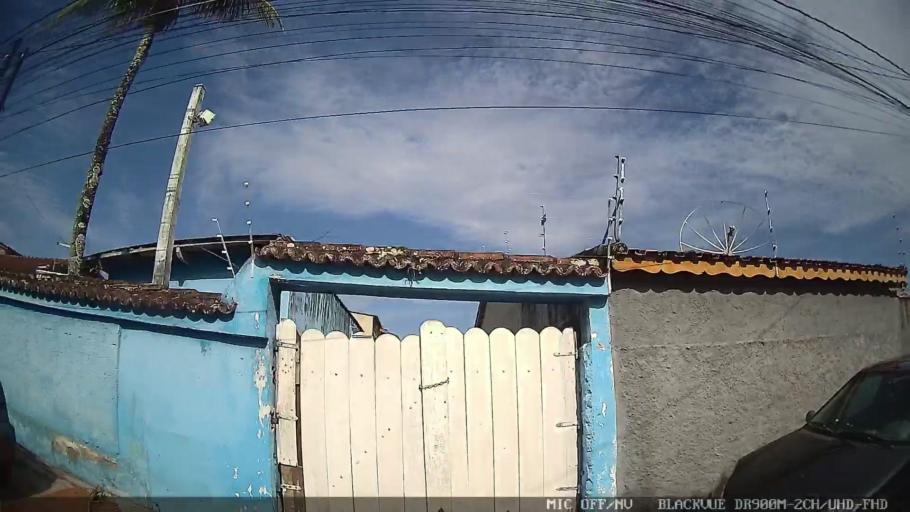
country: BR
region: Sao Paulo
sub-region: Itanhaem
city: Itanhaem
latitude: -24.1608
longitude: -46.7553
